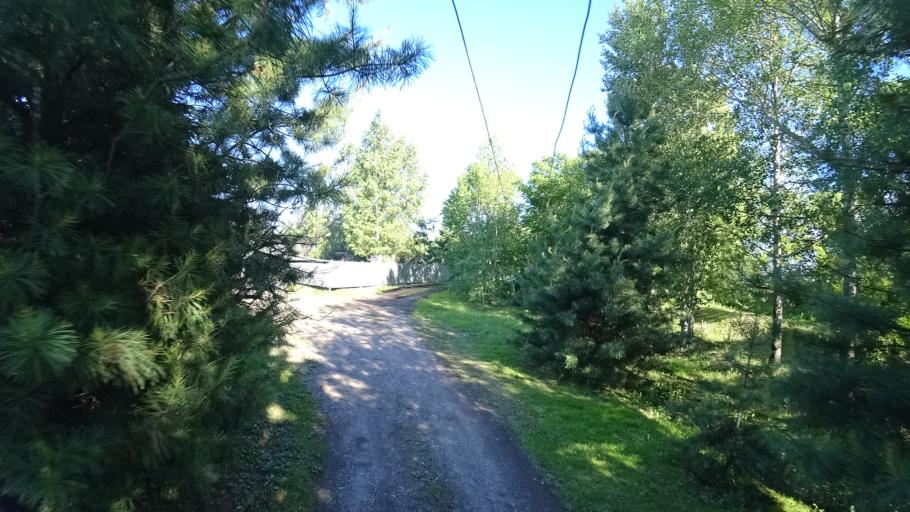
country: RU
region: Khabarovsk Krai
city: Khor
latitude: 47.8930
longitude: 134.9922
